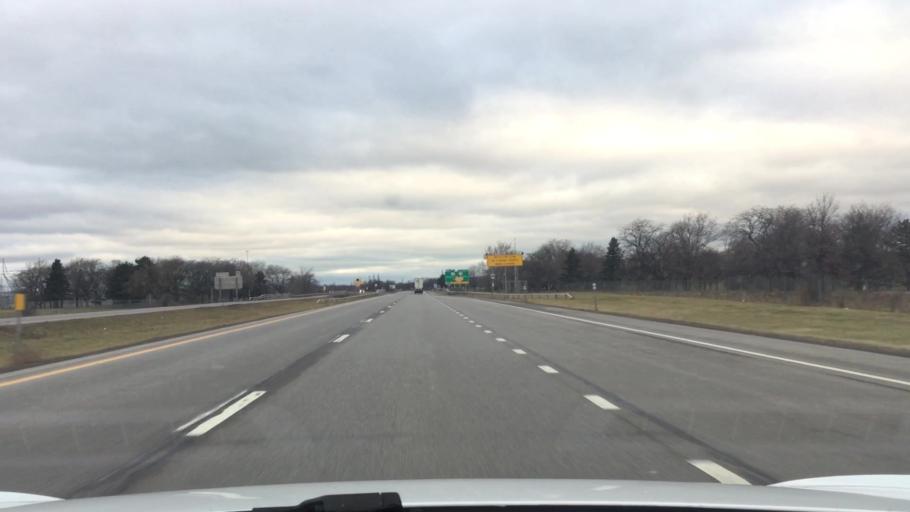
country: US
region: New York
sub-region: Niagara County
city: Lewiston
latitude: 43.1337
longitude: -79.0198
